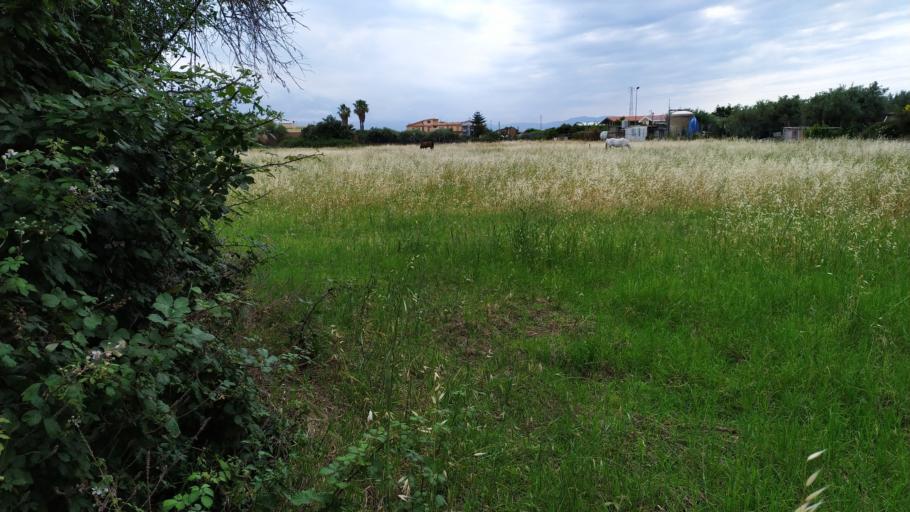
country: IT
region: Sicily
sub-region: Messina
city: San Filippo del Mela
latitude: 38.1815
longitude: 15.2643
